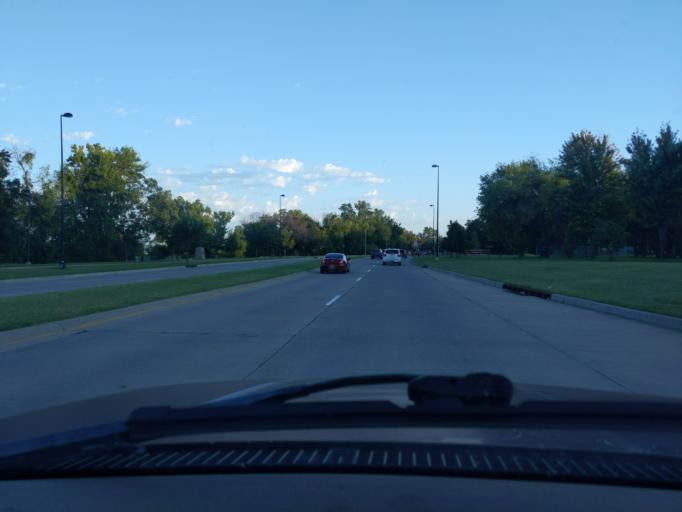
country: US
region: Oklahoma
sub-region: Tulsa County
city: Tulsa
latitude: 36.0919
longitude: -95.9844
